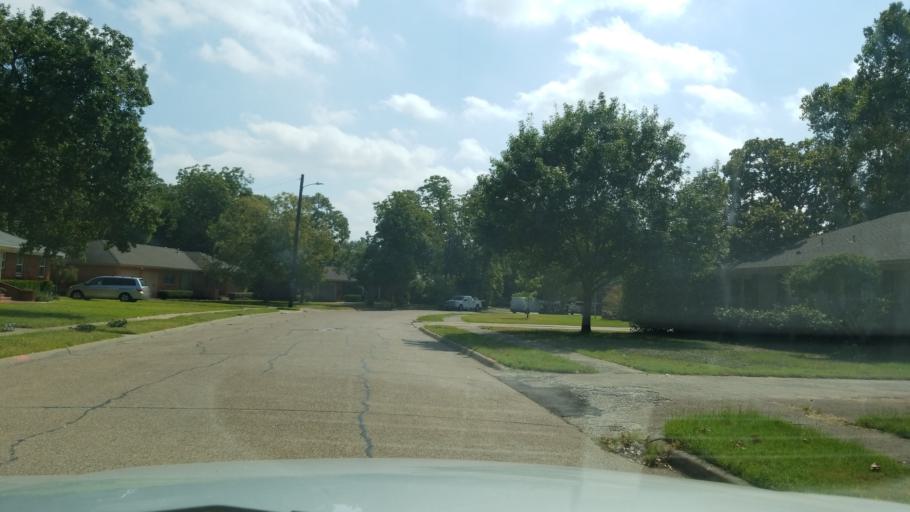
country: US
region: Texas
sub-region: Dallas County
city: Garland
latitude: 32.8958
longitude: -96.6607
